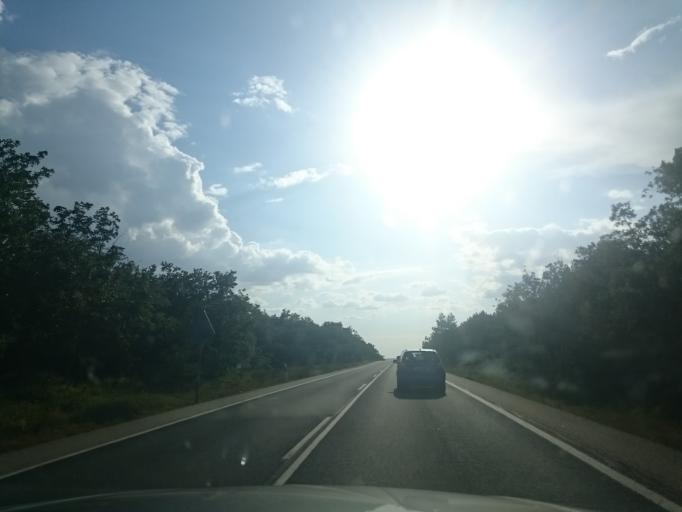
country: ES
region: Castille and Leon
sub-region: Provincia de Burgos
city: Arlanzon
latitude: 42.3509
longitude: -3.4148
